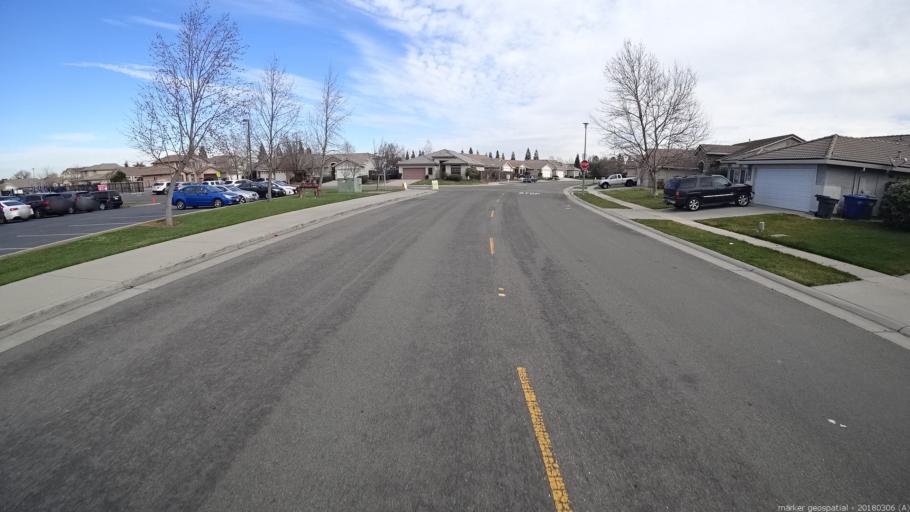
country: US
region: California
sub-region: Sacramento County
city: Vineyard
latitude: 38.4707
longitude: -121.3233
